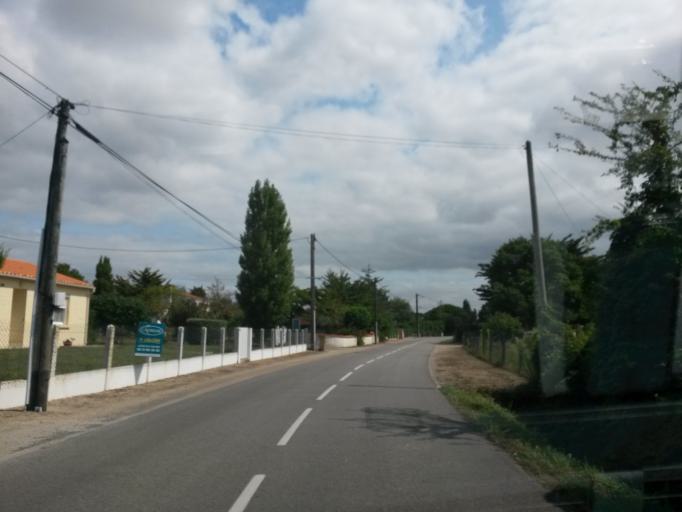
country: FR
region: Pays de la Loire
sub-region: Departement de la Vendee
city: Jard-sur-Mer
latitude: 46.4353
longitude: -1.5830
